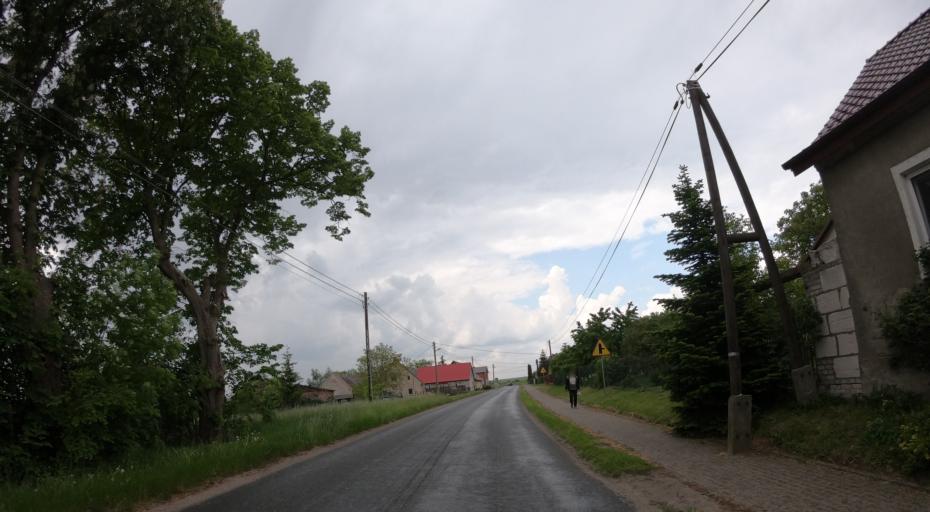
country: PL
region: West Pomeranian Voivodeship
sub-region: Powiat pyrzycki
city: Bielice
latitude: 53.2349
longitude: 14.7290
